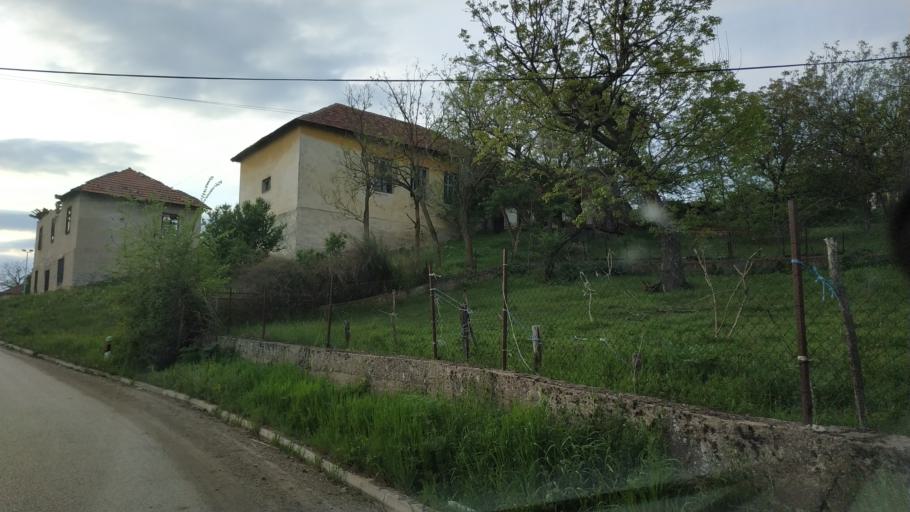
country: RS
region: Central Serbia
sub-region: Zajecarski Okrug
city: Soko Banja
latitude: 43.5279
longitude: 21.8548
